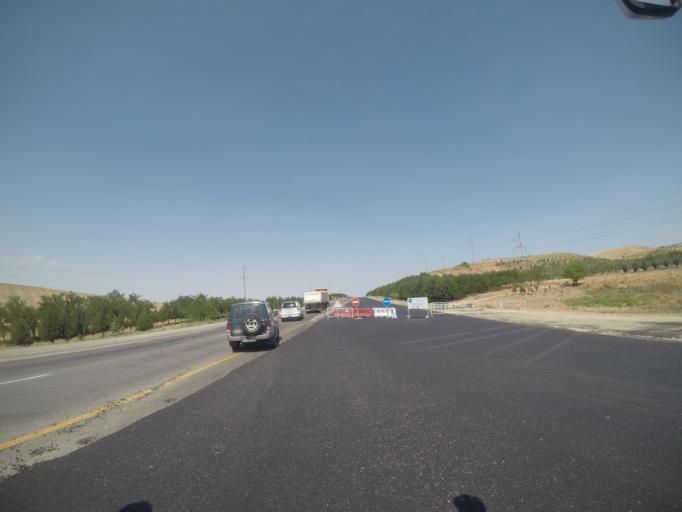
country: AZ
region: Haciqabul
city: Haciqabul
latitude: 40.0443
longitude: 48.9718
